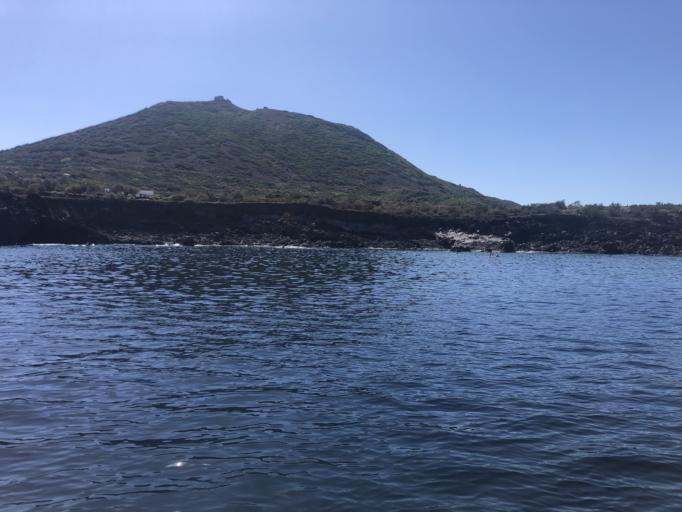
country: IT
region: Sicily
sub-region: Agrigento
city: Lampedusa
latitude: 35.8700
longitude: 12.8806
